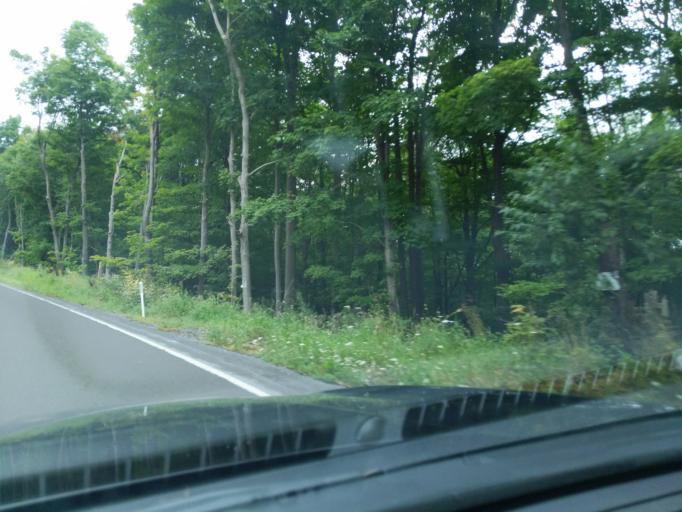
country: US
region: Pennsylvania
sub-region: Blair County
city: Claysburg
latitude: 40.3556
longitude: -78.5166
